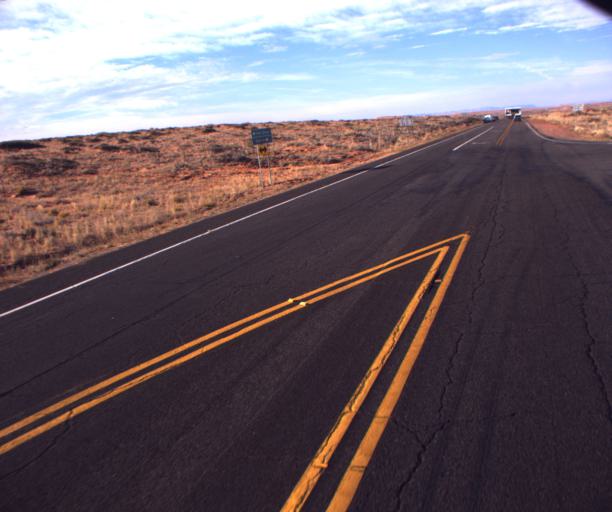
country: US
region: Arizona
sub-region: Apache County
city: Many Farms
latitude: 36.9306
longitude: -109.5742
